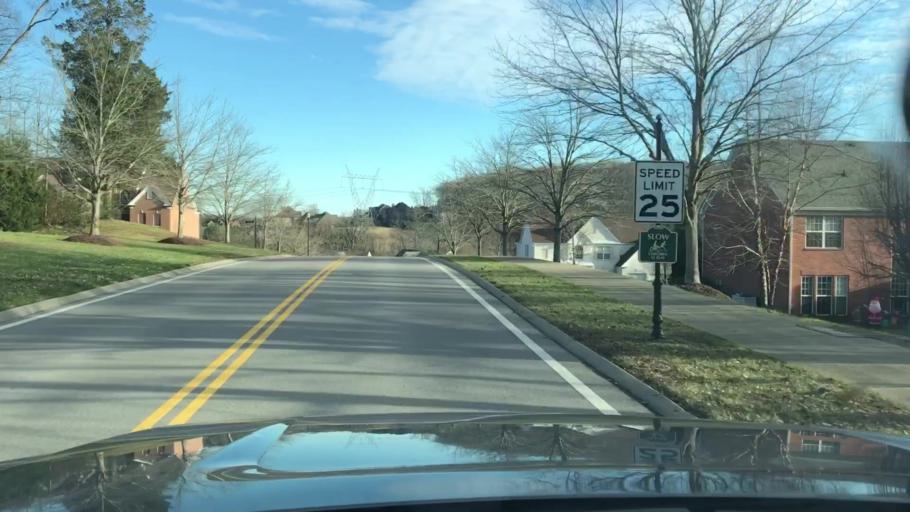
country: US
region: Tennessee
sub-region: Williamson County
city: Brentwood Estates
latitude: 35.9733
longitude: -86.7409
